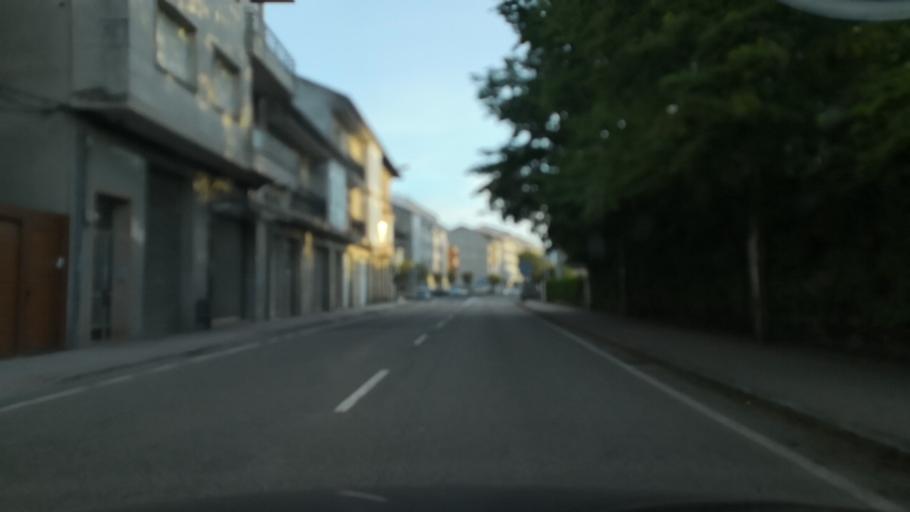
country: ES
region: Galicia
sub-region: Provincia de Ourense
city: Verin
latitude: 41.9353
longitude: -7.4387
